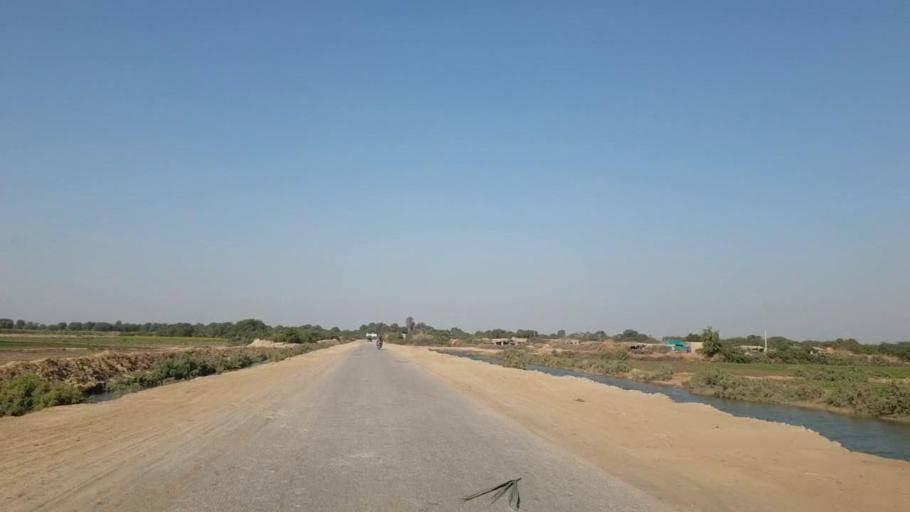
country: PK
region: Sindh
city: Digri
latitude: 25.1187
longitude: 69.1083
